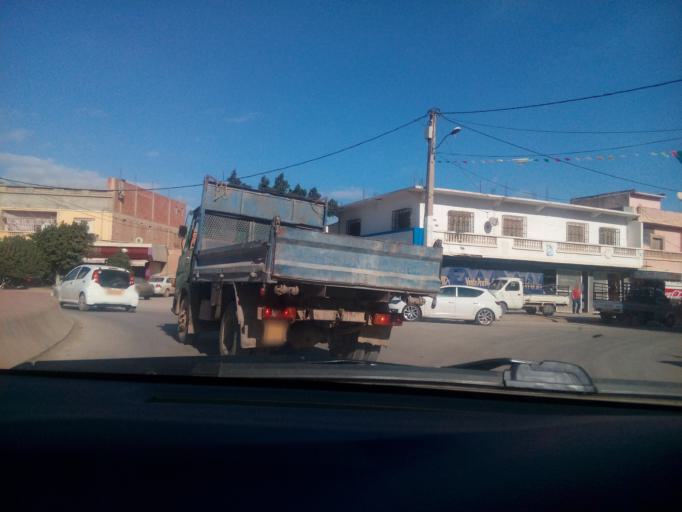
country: DZ
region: Oran
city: Sidi ech Chahmi
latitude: 35.6524
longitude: -0.5676
